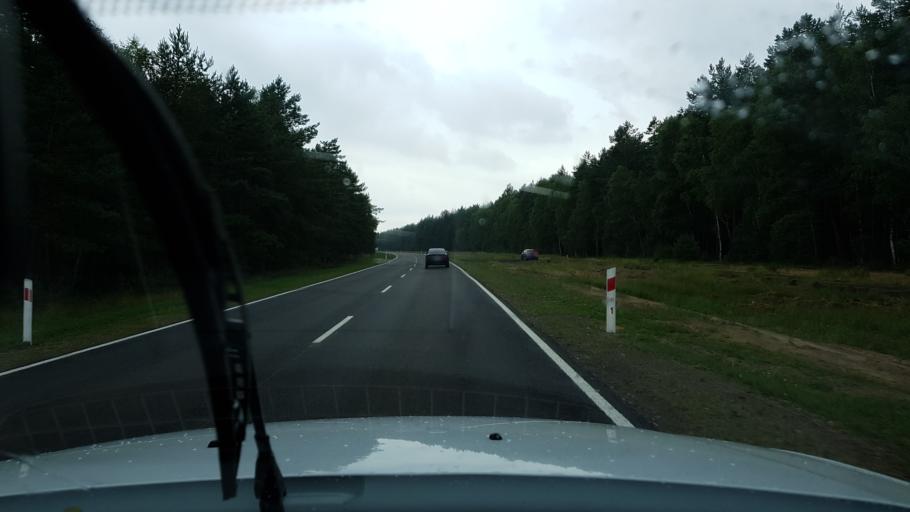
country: PL
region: West Pomeranian Voivodeship
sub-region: Powiat stargardzki
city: Kobylanka
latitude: 53.4352
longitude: 14.8602
